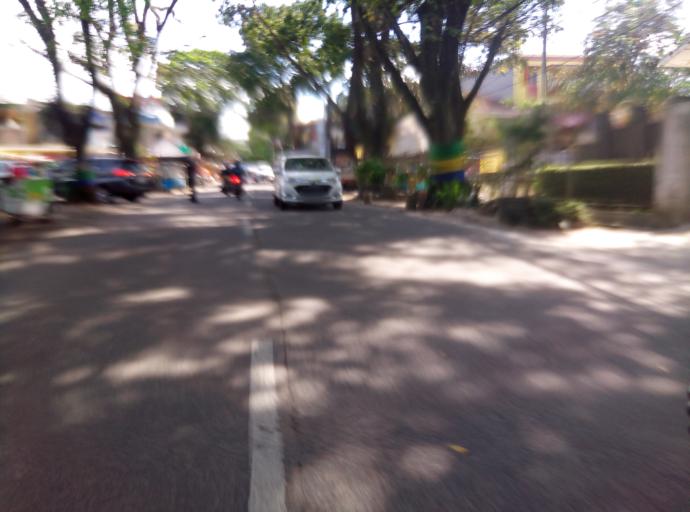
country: ID
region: West Java
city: Bandung
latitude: -6.8851
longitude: 107.6191
